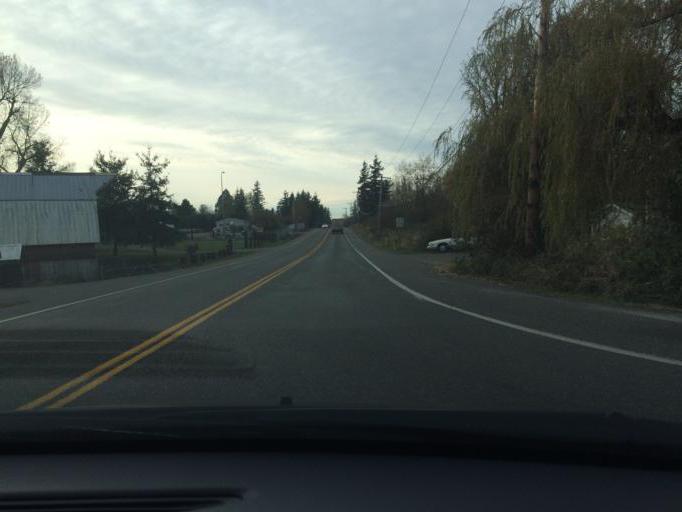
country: US
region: Washington
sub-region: Whatcom County
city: Marietta-Alderwood
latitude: 48.8169
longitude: -122.5285
